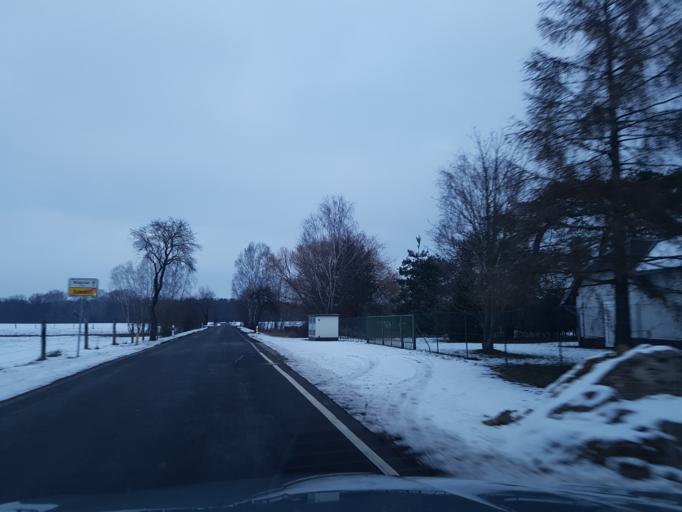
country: DE
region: Brandenburg
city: Schilda
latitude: 51.5781
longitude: 13.4042
